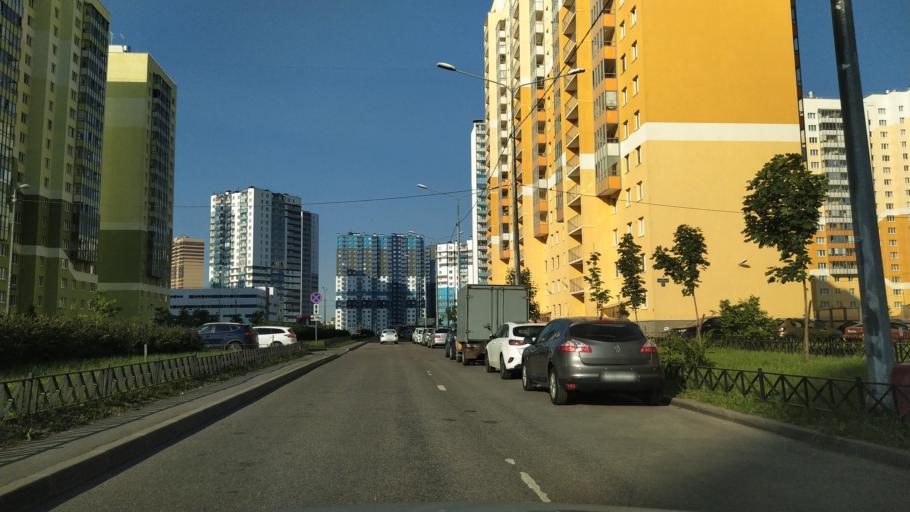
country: RU
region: Leningrad
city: Murino
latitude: 60.0340
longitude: 30.4508
